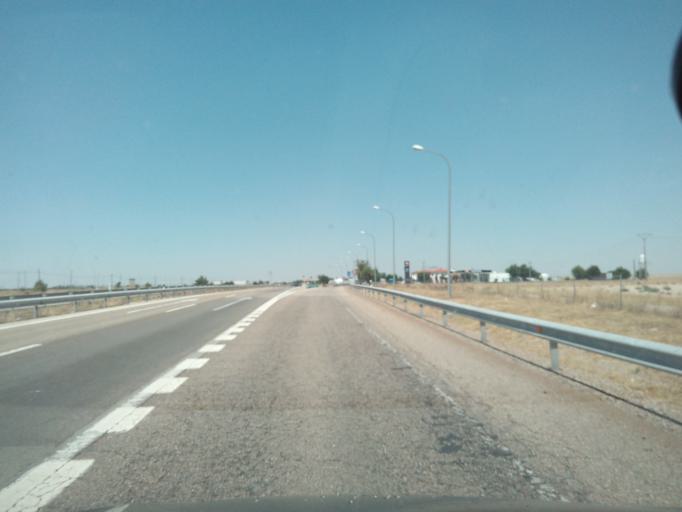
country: ES
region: Castille-La Mancha
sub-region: Province of Toledo
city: Tembleque
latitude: 39.7633
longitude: -3.4809
